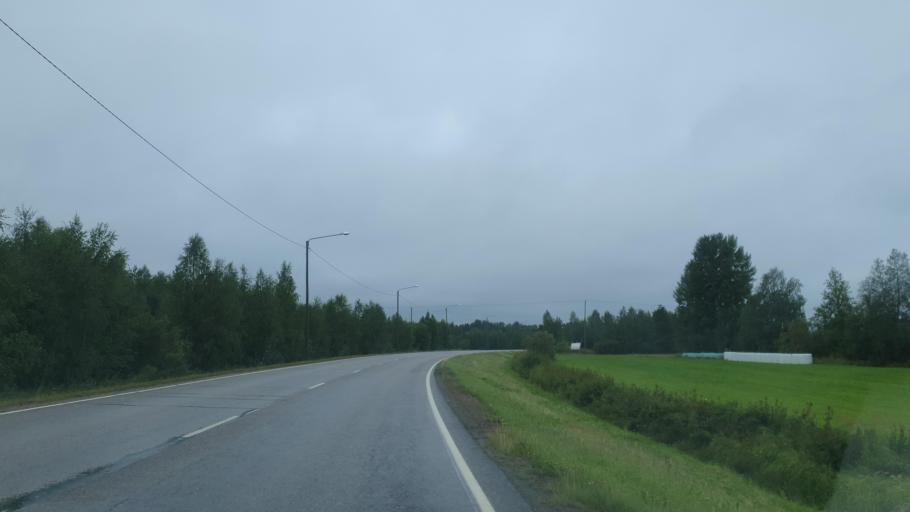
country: FI
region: Lapland
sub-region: Itae-Lappi
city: Kemijaervi
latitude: 66.6935
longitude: 27.5737
